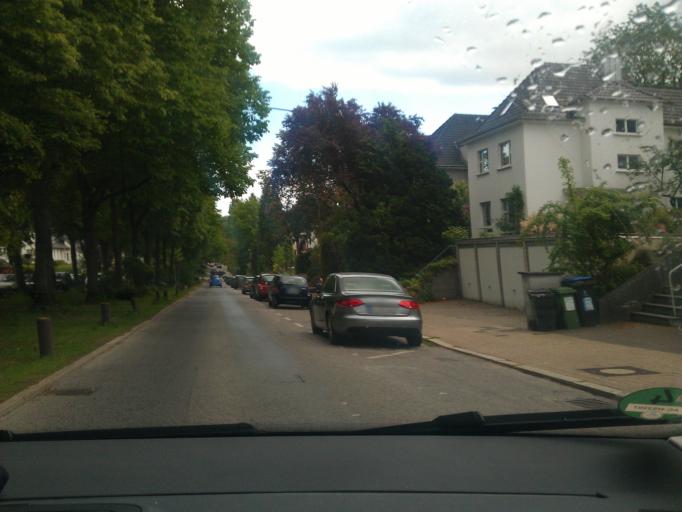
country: DE
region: North Rhine-Westphalia
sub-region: Regierungsbezirk Koln
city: Aachen
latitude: 50.7565
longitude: 6.0861
